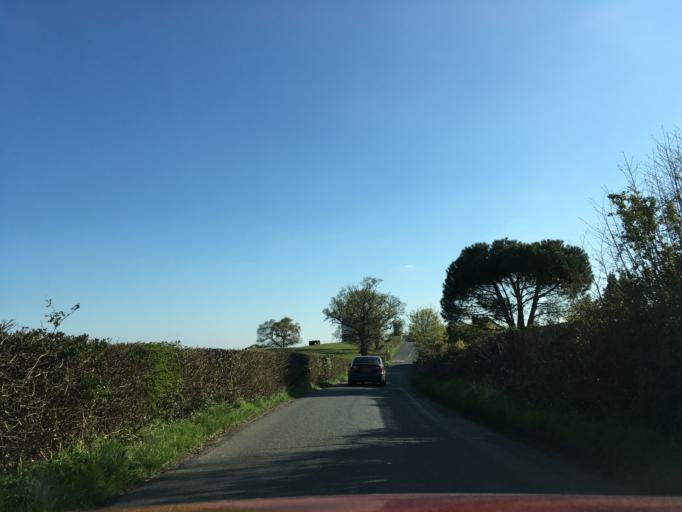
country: GB
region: Wales
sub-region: Torfaen County Borough
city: New Inn
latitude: 51.6968
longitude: -2.9993
